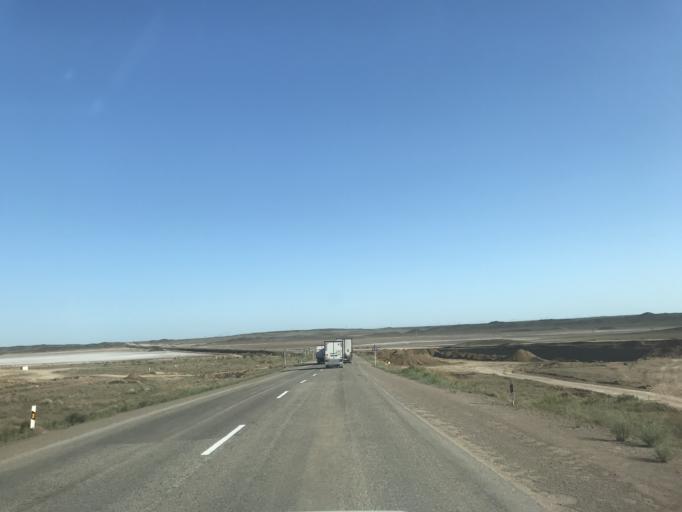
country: KZ
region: Zhambyl
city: Mynaral
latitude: 45.3219
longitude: 73.7406
